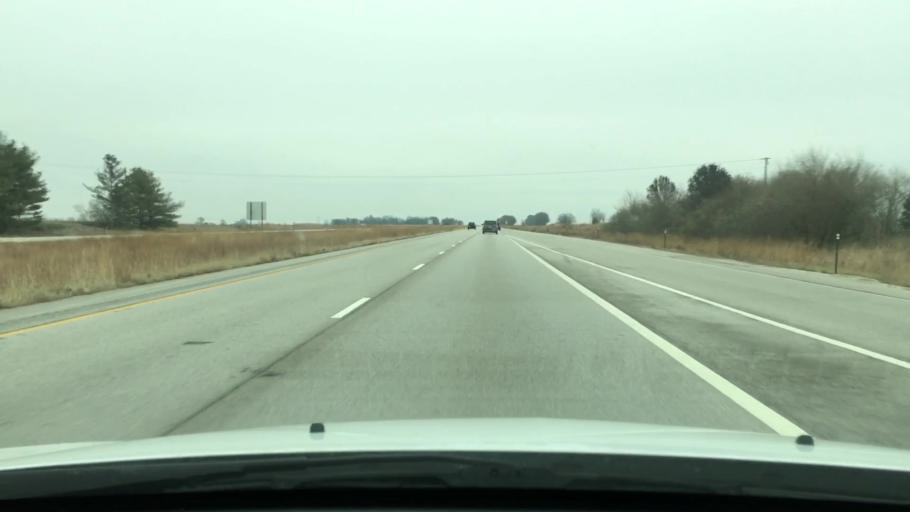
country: US
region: Illinois
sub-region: Sangamon County
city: New Berlin
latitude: 39.7368
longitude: -90.0372
